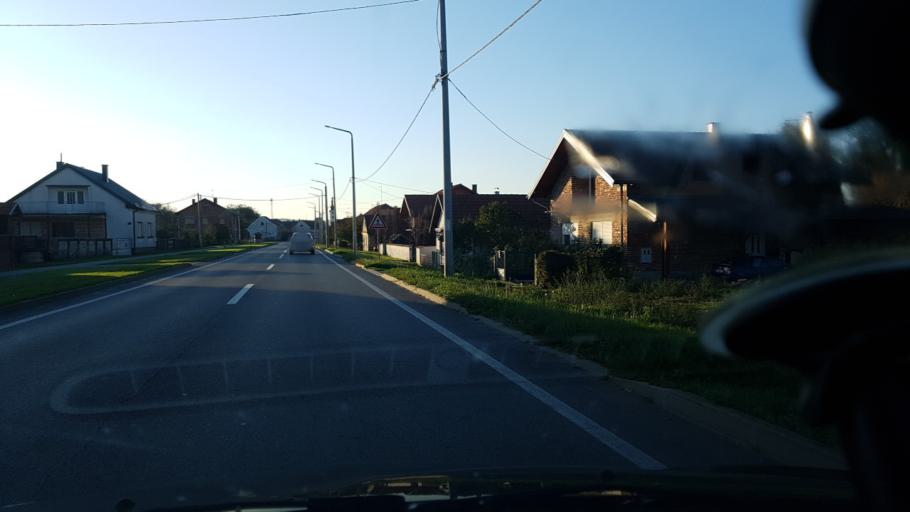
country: HR
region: Koprivnicko-Krizevacka
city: Virje
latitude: 46.0736
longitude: 16.9570
